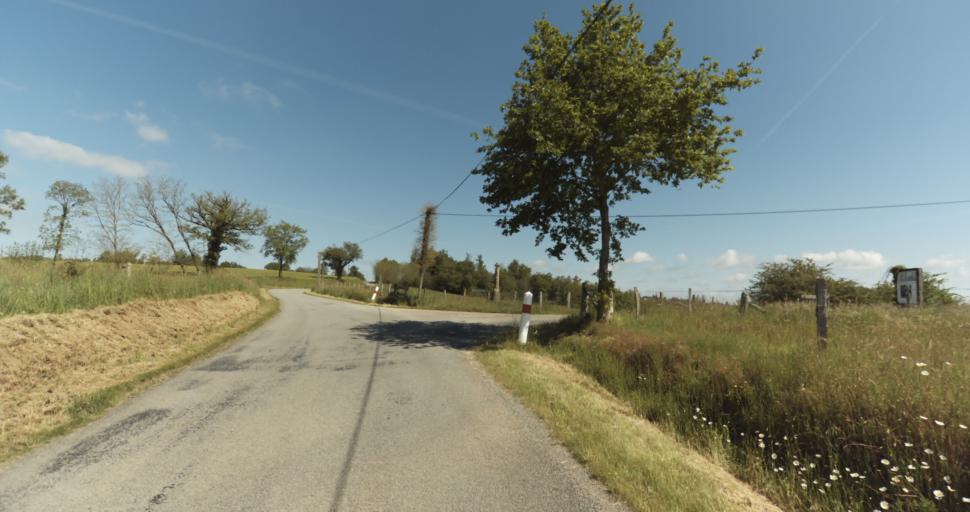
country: FR
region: Limousin
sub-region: Departement de la Haute-Vienne
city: Le Vigen
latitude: 45.7076
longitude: 1.2999
